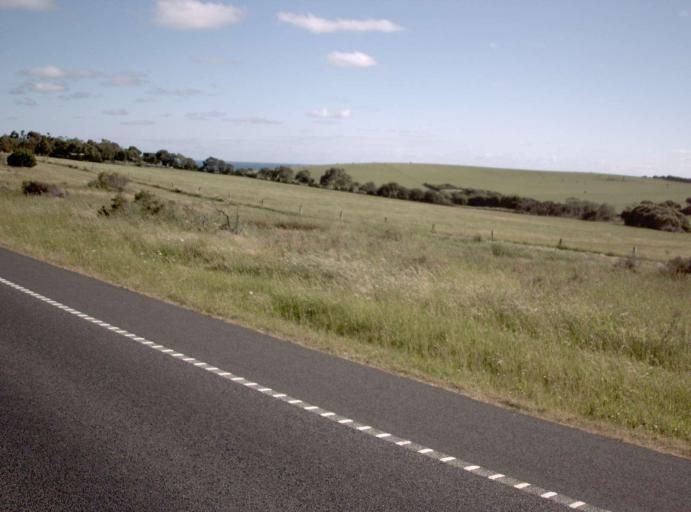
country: AU
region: Victoria
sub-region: Bass Coast
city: North Wonthaggi
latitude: -38.5376
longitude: 145.4566
